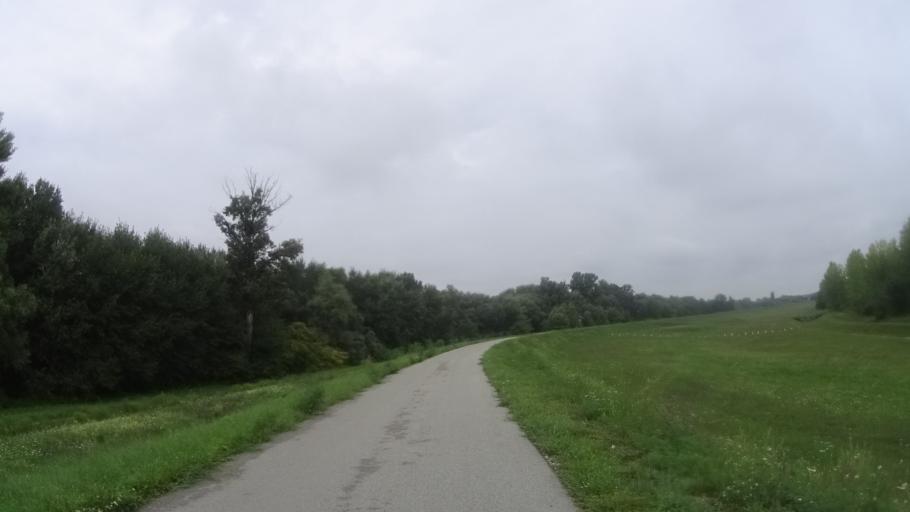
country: SK
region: Nitriansky
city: Komarno
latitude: 47.7533
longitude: 18.1481
